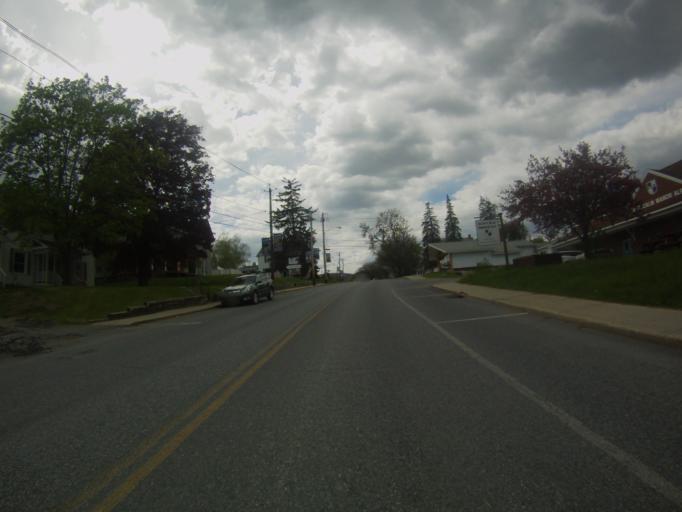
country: US
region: New York
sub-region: Essex County
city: Ticonderoga
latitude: 43.8482
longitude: -73.4300
